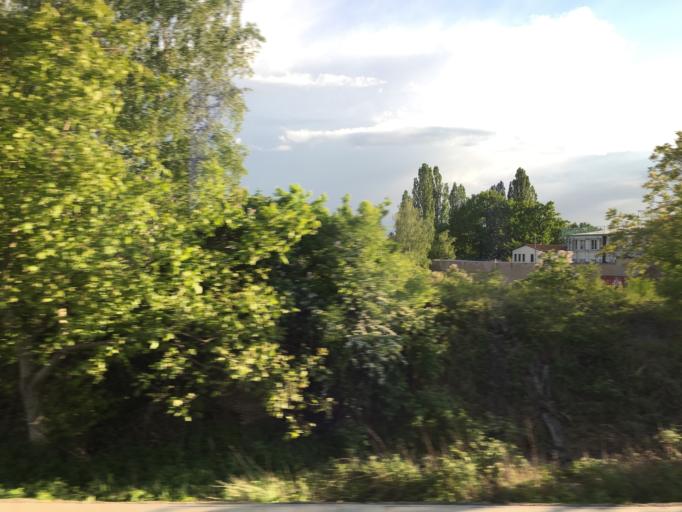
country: DE
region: Saxony
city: Radebeul
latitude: 51.0934
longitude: 13.6931
